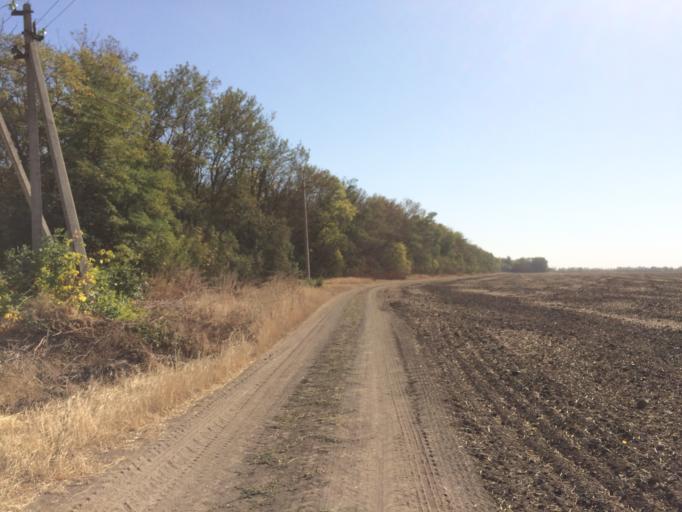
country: RU
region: Rostov
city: Tselina
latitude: 46.5279
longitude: 41.1810
